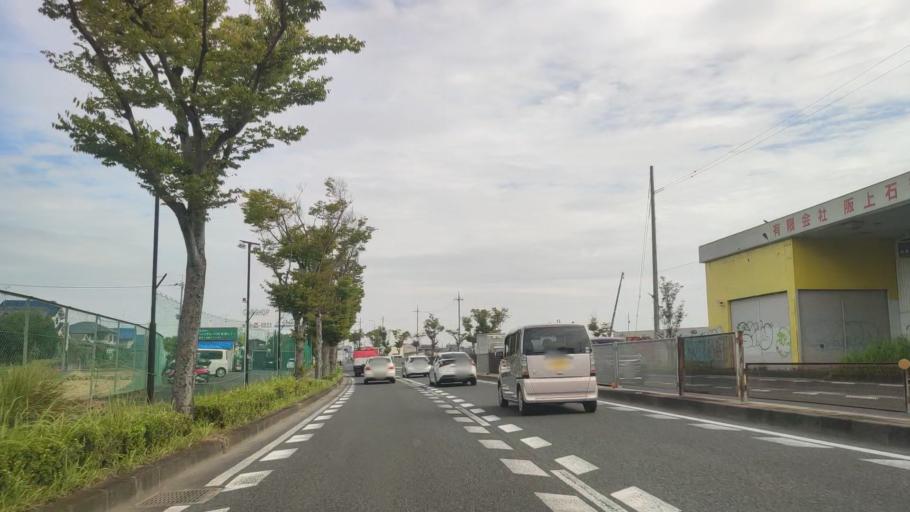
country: JP
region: Osaka
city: Tondabayashicho
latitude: 34.5148
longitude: 135.6047
